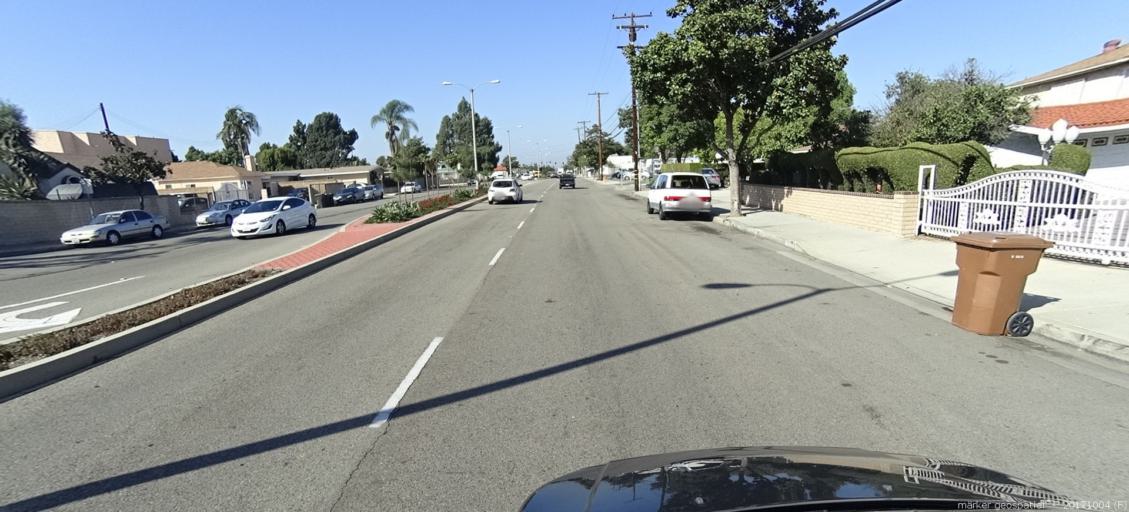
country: US
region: California
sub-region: Orange County
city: Stanton
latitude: 33.7857
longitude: -117.9754
